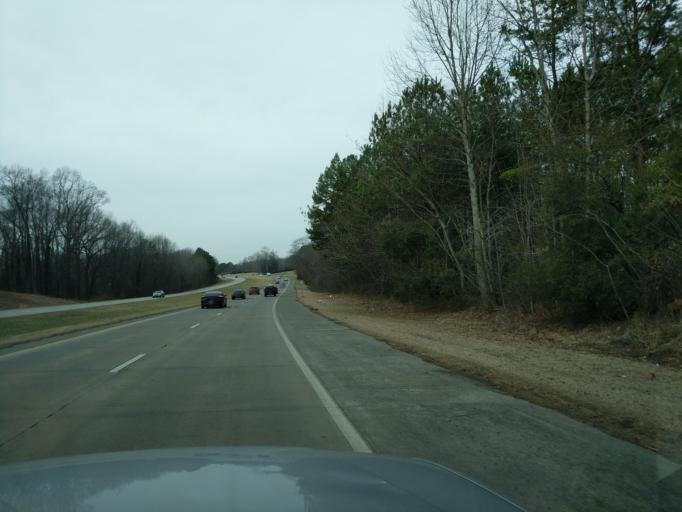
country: US
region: North Carolina
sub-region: Mecklenburg County
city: Charlotte
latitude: 35.1824
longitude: -80.8936
